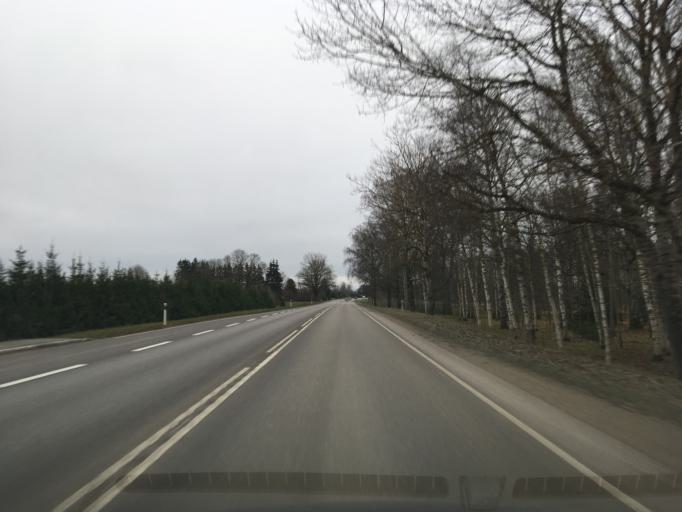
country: EE
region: Laeaene-Virumaa
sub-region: Rakvere linn
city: Rakvere
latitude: 59.3952
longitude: 26.3820
